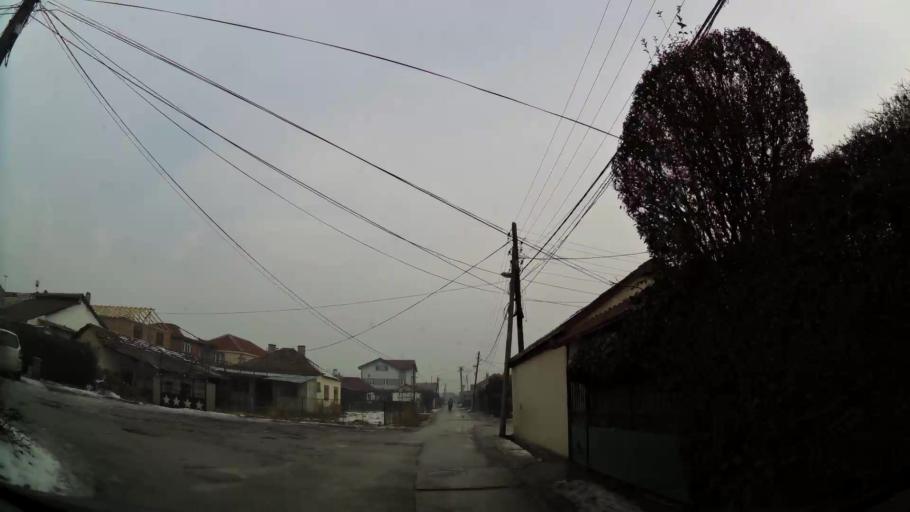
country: MK
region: Ilinden
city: Jurumleri
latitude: 41.9667
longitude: 21.5610
